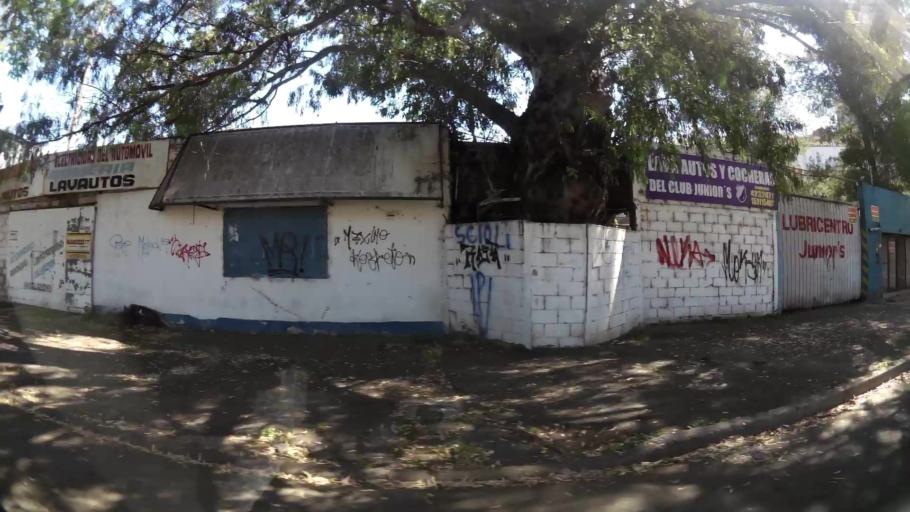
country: AR
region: Cordoba
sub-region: Departamento de Capital
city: Cordoba
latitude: -31.4212
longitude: -64.1690
